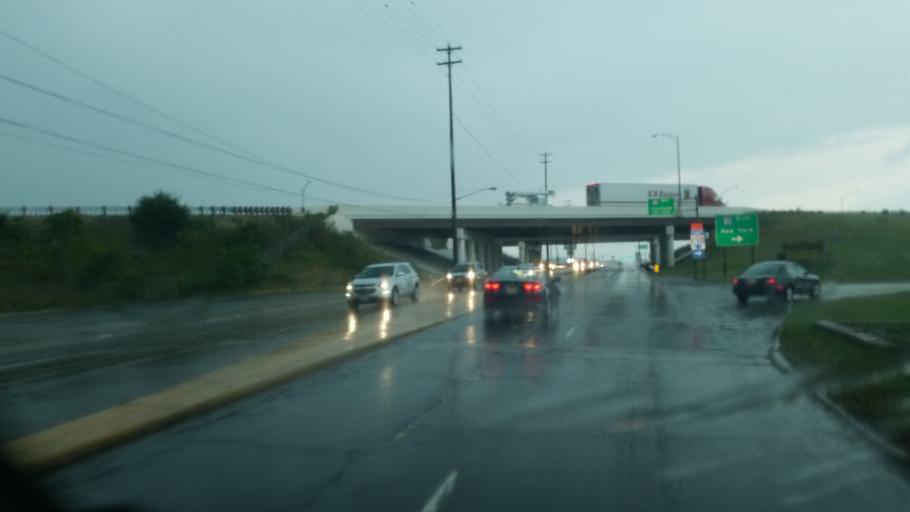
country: US
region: Ohio
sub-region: Trumbull County
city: Churchill
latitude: 41.1543
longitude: -80.6649
